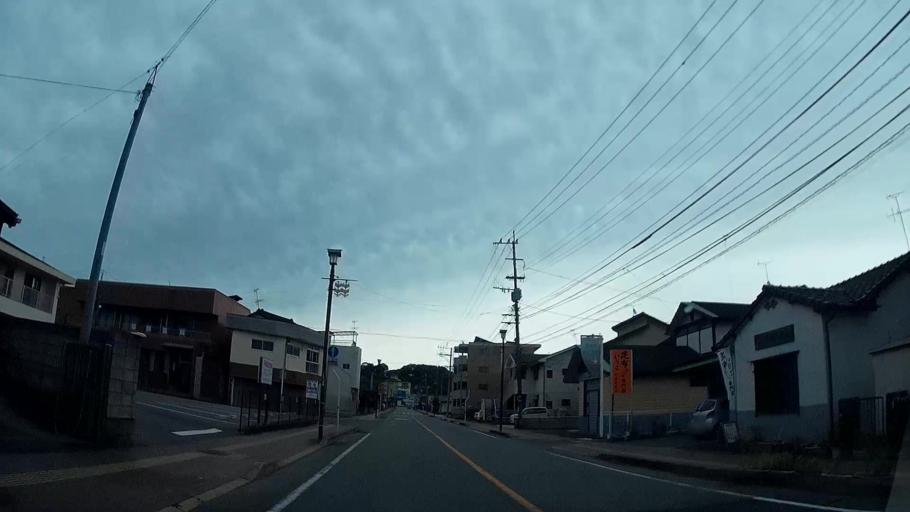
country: JP
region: Kumamoto
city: Kikuchi
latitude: 32.9812
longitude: 130.8126
